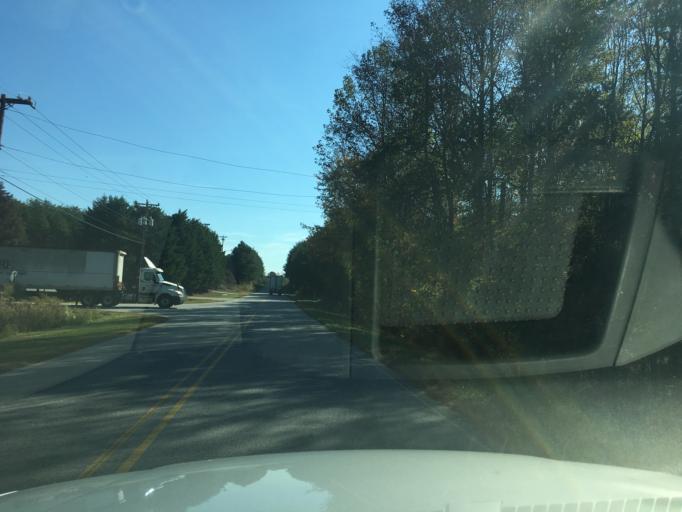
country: US
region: North Carolina
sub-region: Catawba County
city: Conover
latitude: 35.7153
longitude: -81.2597
